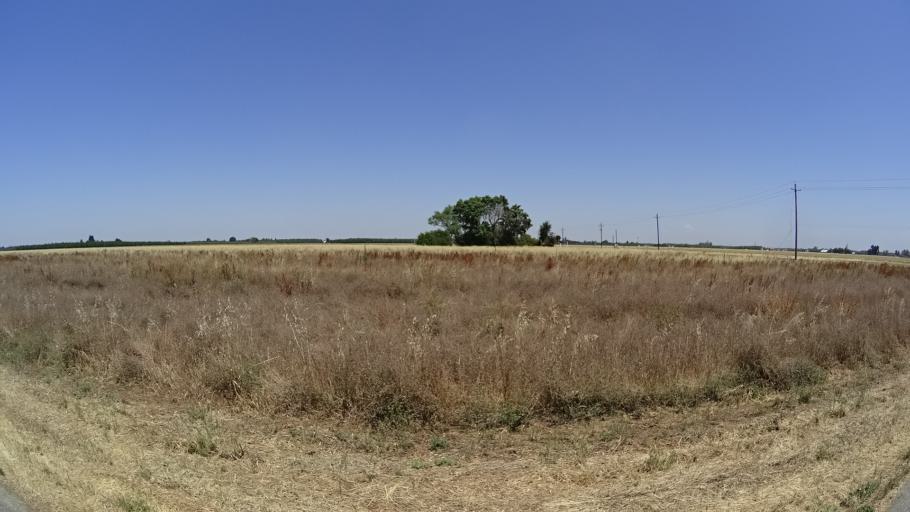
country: US
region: California
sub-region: Fresno County
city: Laton
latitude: 36.3863
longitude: -119.7276
